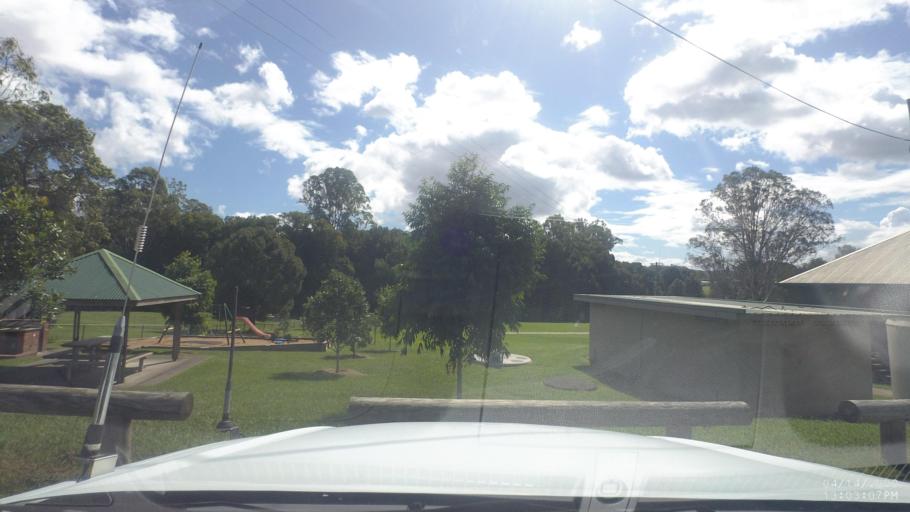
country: AU
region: Queensland
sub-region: Gold Coast
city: Ormeau Hills
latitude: -27.8271
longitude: 153.1794
